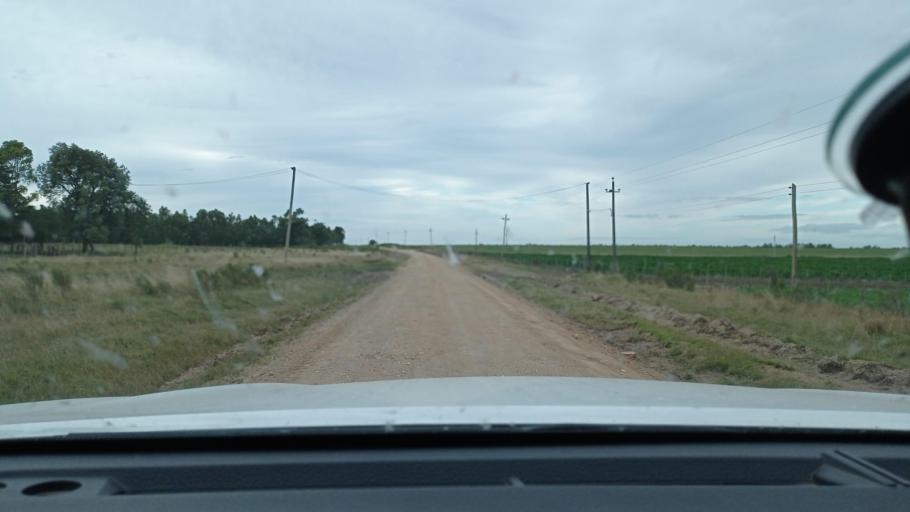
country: UY
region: Florida
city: Casupa
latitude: -34.1115
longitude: -55.7658
